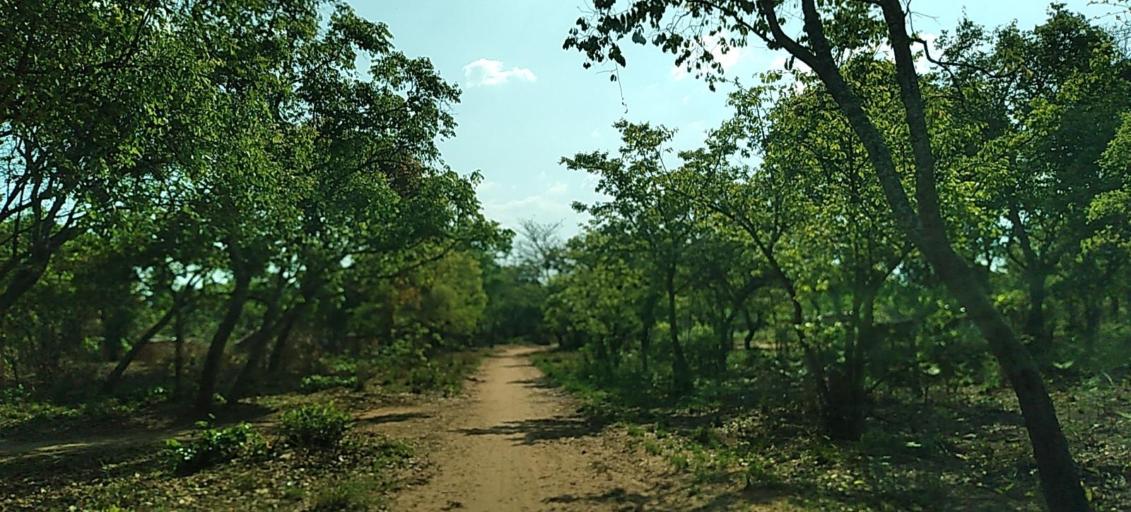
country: ZM
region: North-Western
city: Mwinilunga
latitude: -11.2998
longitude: 24.8515
